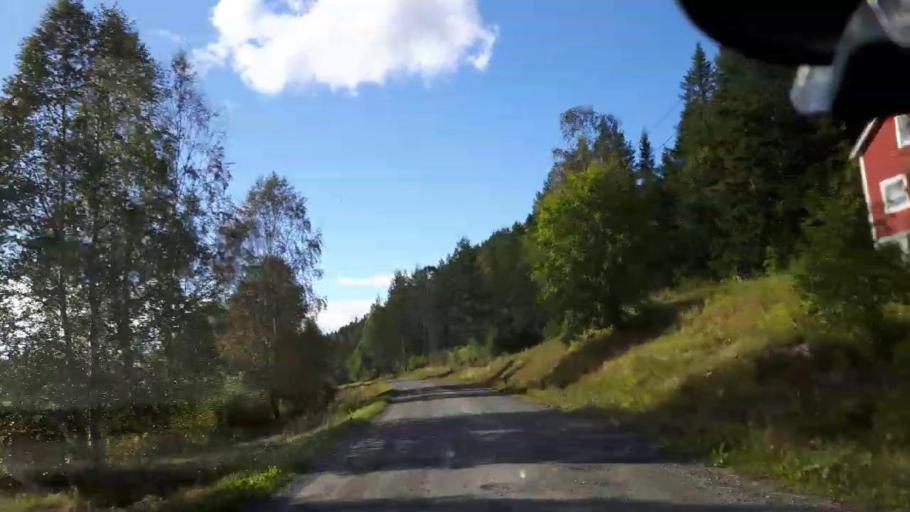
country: SE
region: Jaemtland
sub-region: Ragunda Kommun
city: Hammarstrand
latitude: 63.4752
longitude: 16.1661
